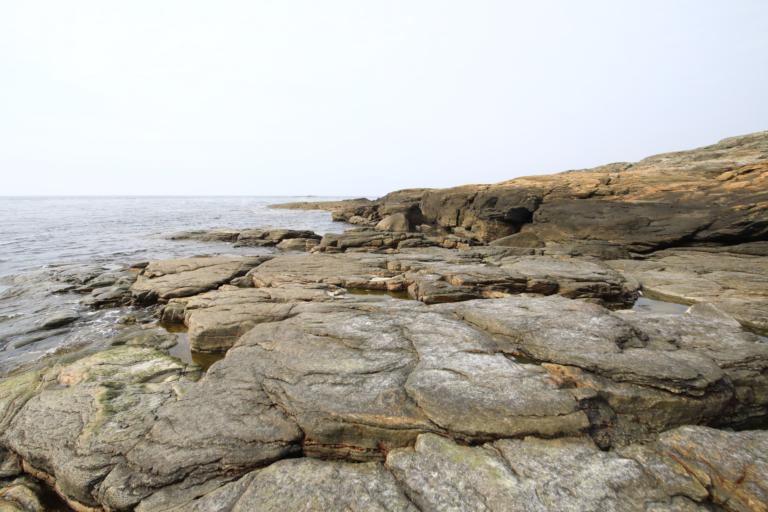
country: SE
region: Halland
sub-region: Kungsbacka Kommun
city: Frillesas
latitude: 57.2479
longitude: 12.0921
